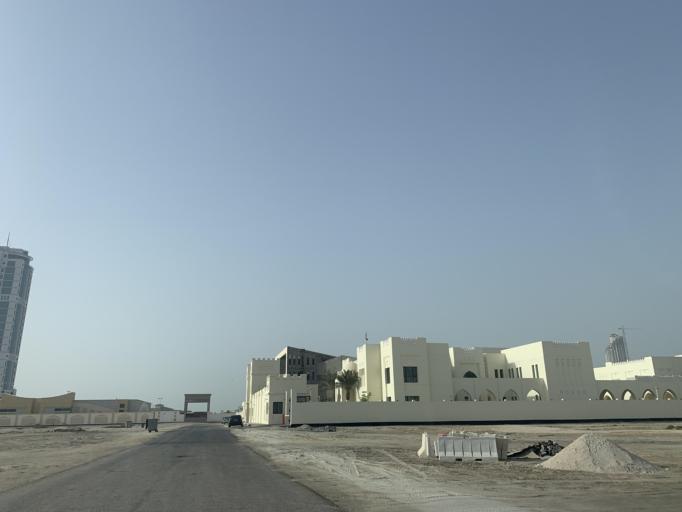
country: BH
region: Manama
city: Jidd Hafs
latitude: 26.2360
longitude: 50.5455
